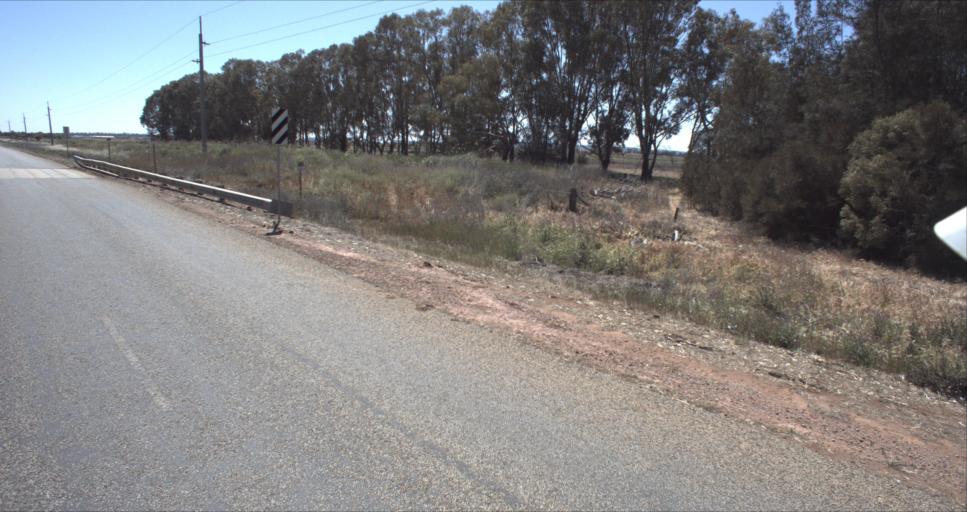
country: AU
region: New South Wales
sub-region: Leeton
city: Leeton
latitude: -34.4652
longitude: 146.2934
